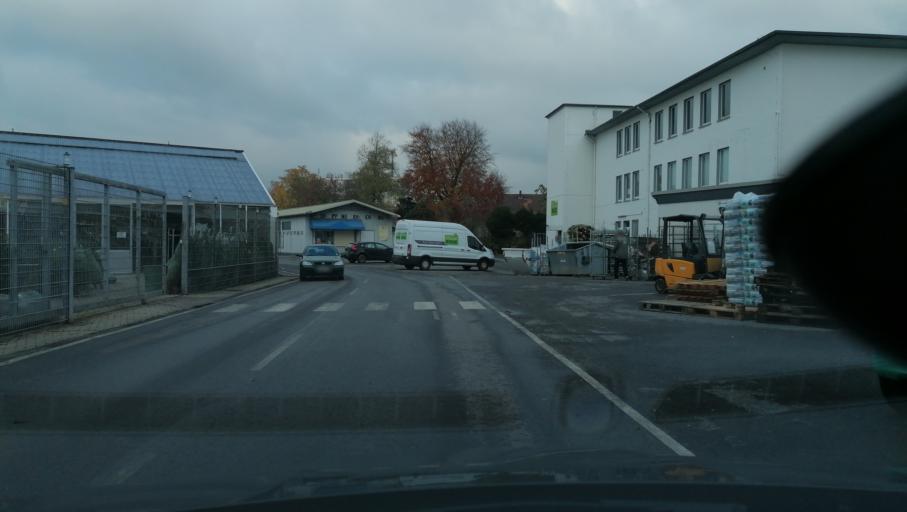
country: DE
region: North Rhine-Westphalia
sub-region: Regierungsbezirk Arnsberg
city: Herne
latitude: 51.5640
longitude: 7.2070
